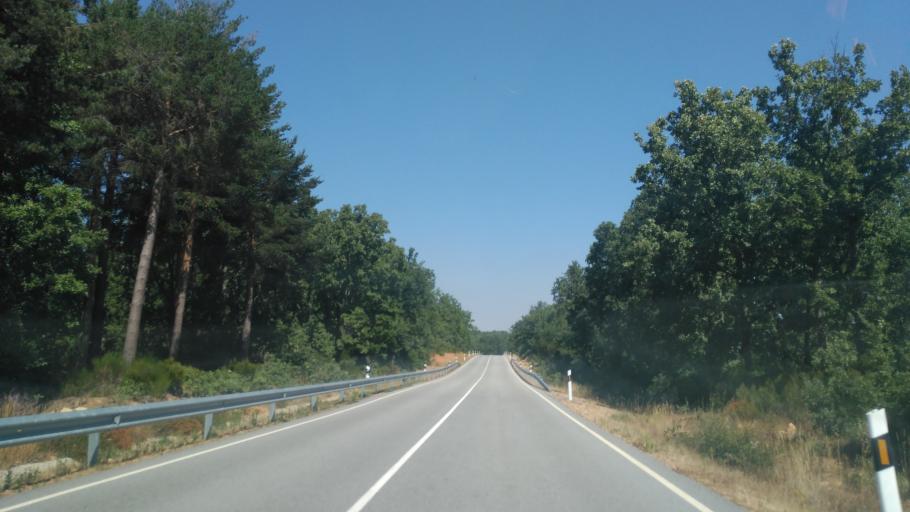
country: ES
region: Castille and Leon
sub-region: Provincia de Salamanca
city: Nava de Francia
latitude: 40.5477
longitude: -6.1349
